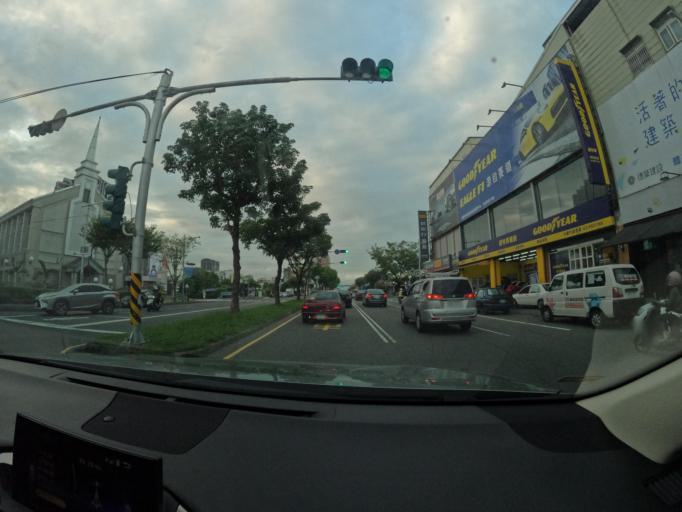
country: TW
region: Taiwan
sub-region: Yilan
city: Yilan
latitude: 24.6719
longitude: 121.7778
